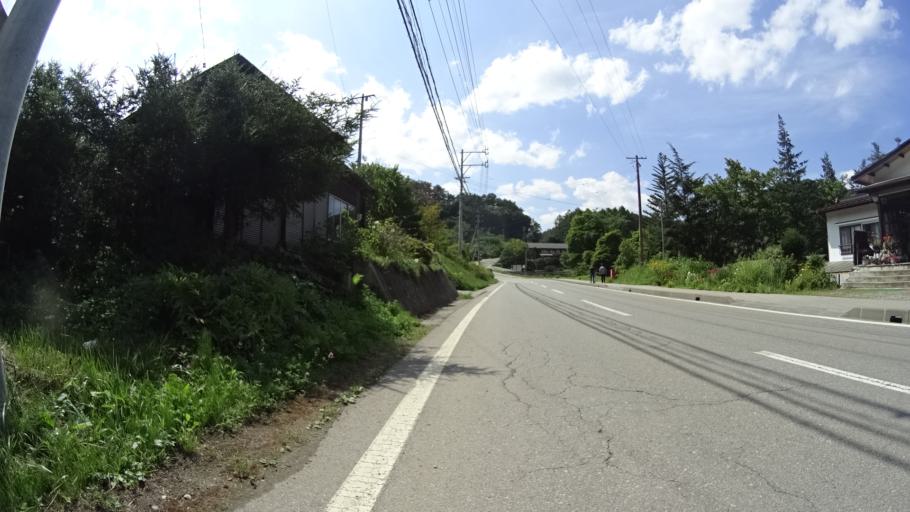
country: JP
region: Nagano
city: Saku
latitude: 36.0508
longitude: 138.4564
